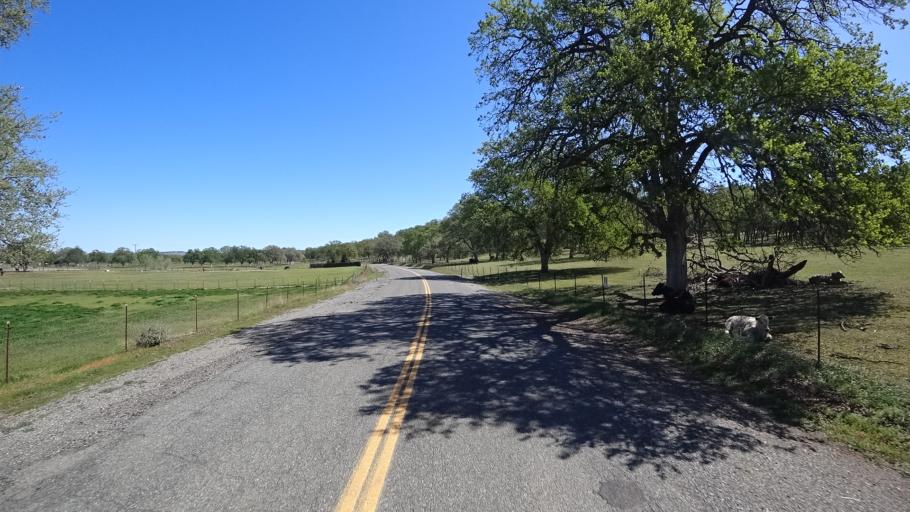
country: US
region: California
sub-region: Glenn County
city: Orland
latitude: 39.7313
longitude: -122.4061
